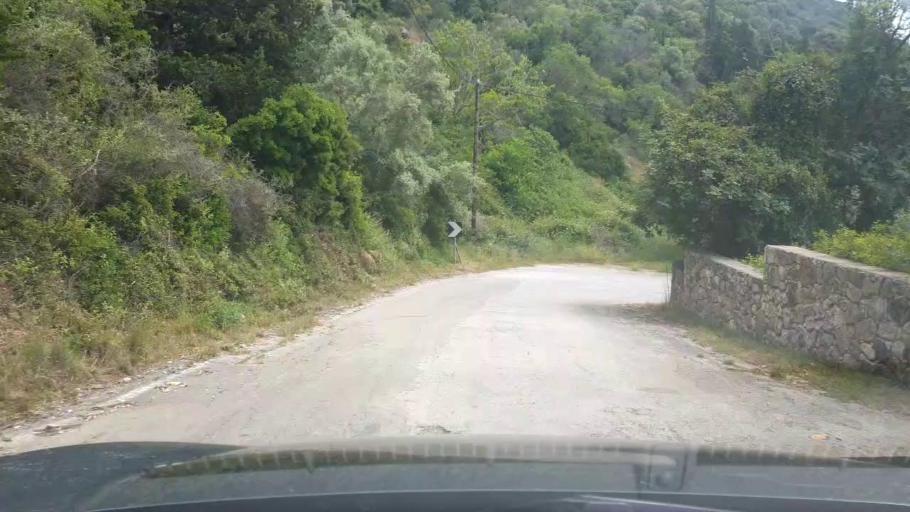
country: GR
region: Ionian Islands
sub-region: Lefkada
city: Nidri
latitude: 38.6444
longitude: 20.7009
